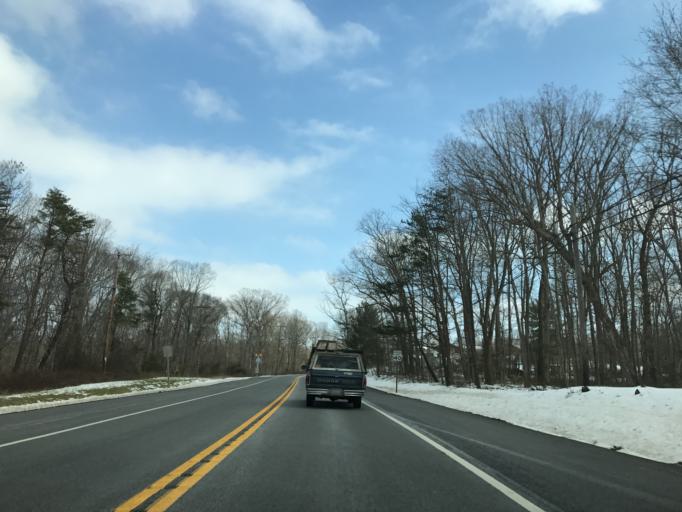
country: US
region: Pennsylvania
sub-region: York County
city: Susquehanna Trails
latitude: 39.6589
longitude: -76.2769
